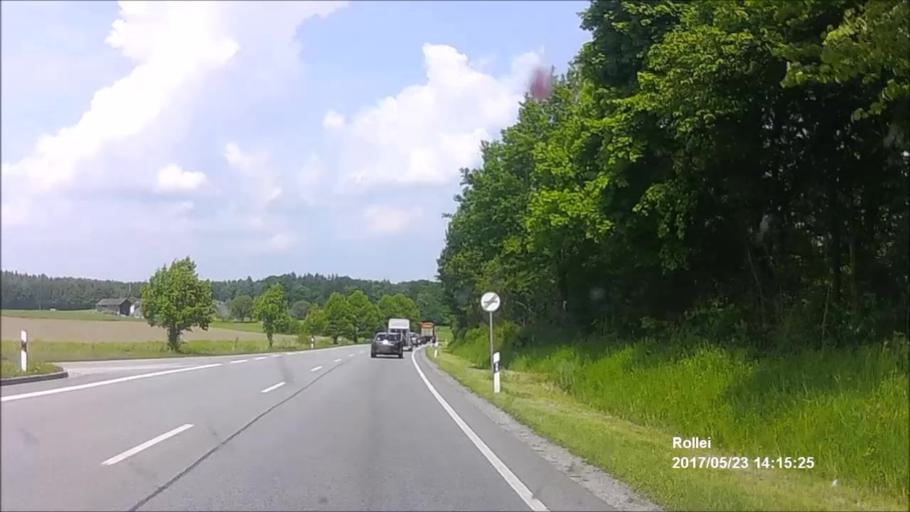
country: DE
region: Bavaria
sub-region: Upper Bavaria
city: Wasserburg am Inn
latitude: 48.0644
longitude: 12.2017
